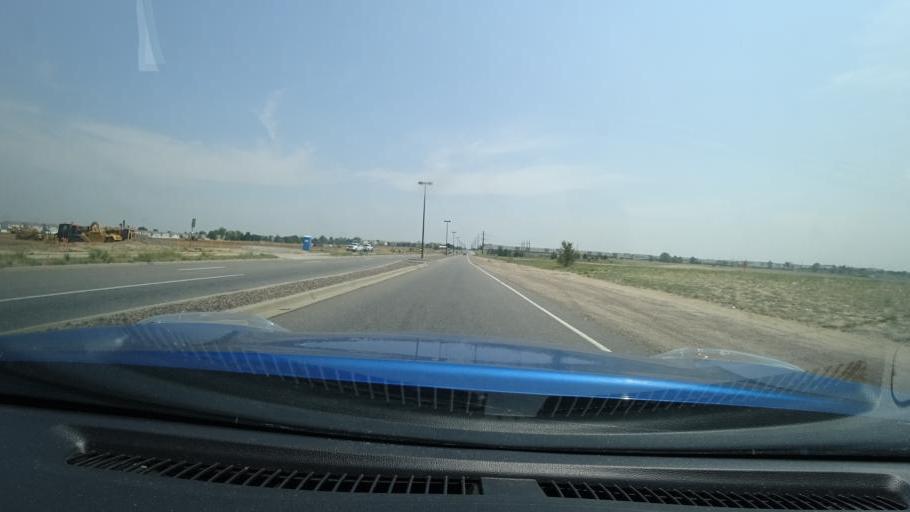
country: US
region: Colorado
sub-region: Adams County
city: Aurora
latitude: 39.7699
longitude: -104.7698
